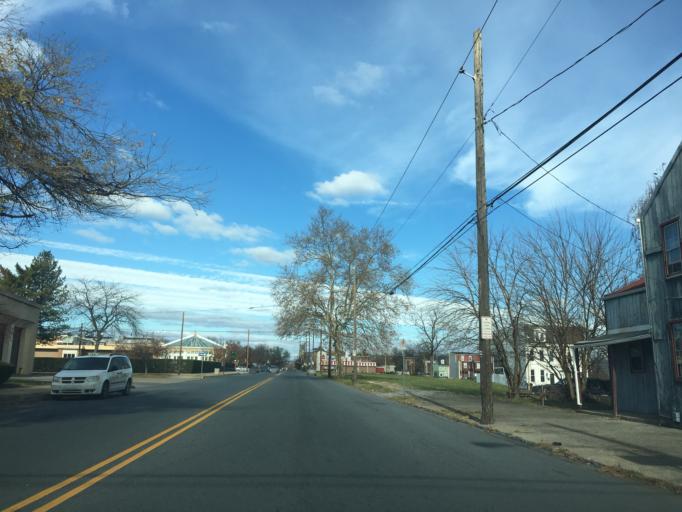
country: US
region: Pennsylvania
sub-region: Dauphin County
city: Harrisburg
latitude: 40.2777
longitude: -76.8889
